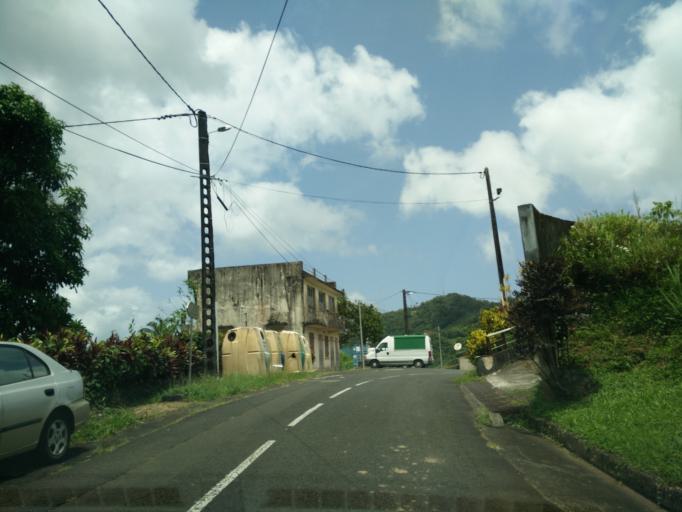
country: MQ
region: Martinique
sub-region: Martinique
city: Le Morne-Rouge
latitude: 14.7367
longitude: -61.1321
